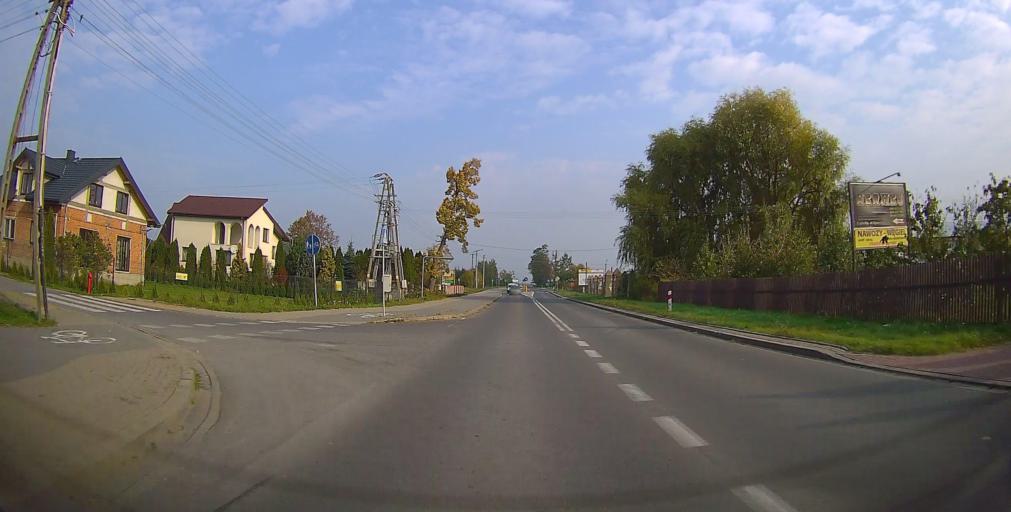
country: PL
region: Masovian Voivodeship
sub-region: Powiat grojecki
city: Mogielnica
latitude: 51.7055
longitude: 20.7371
